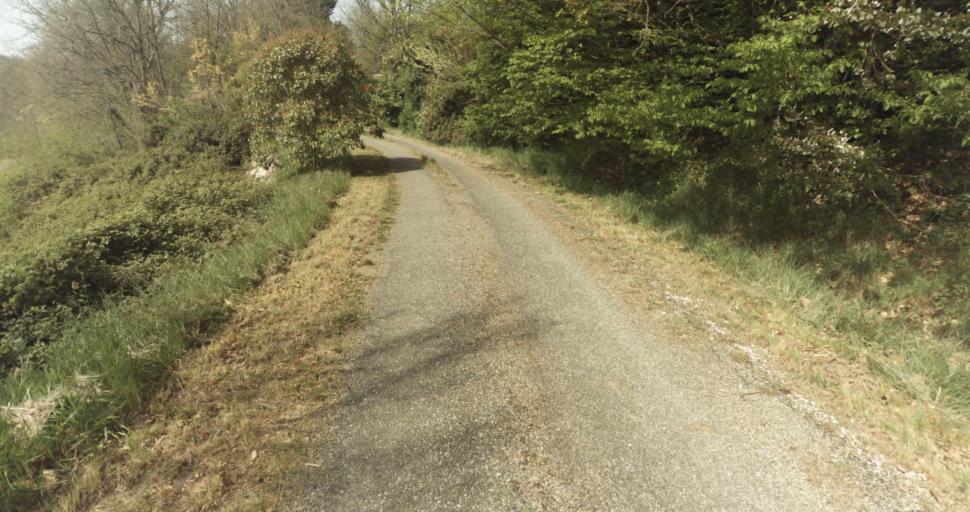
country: FR
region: Midi-Pyrenees
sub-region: Departement du Tarn-et-Garonne
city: Moissac
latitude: 44.1475
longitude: 1.1285
